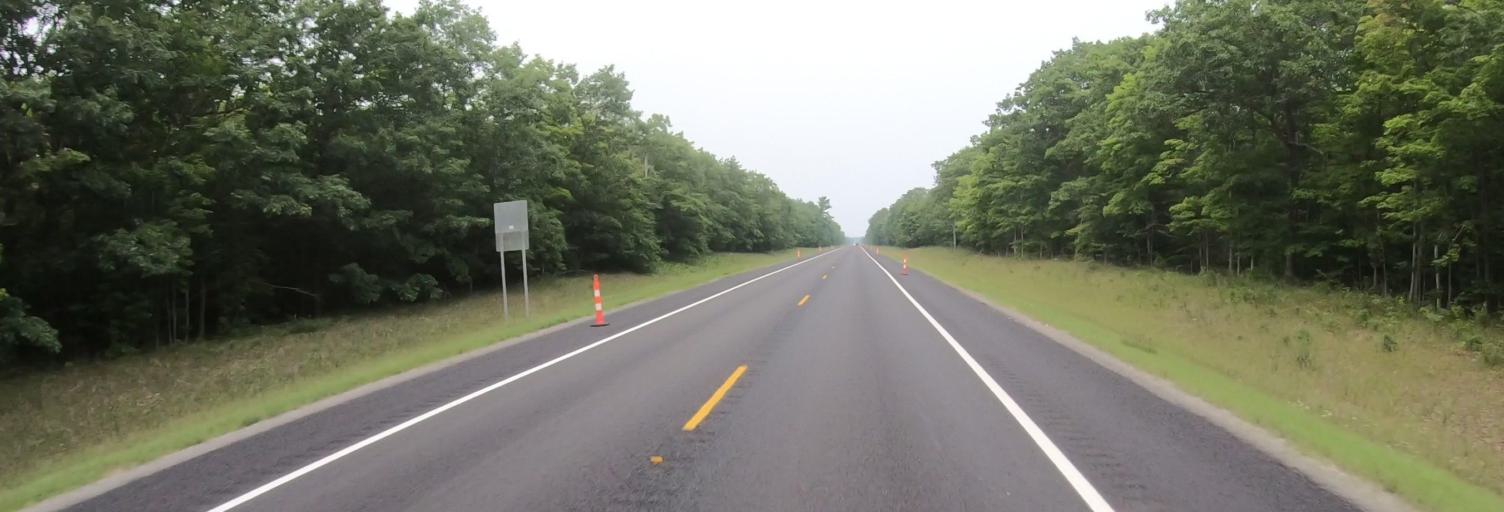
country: US
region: Michigan
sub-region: Mackinac County
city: Saint Ignace
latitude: 45.7097
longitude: -84.7618
